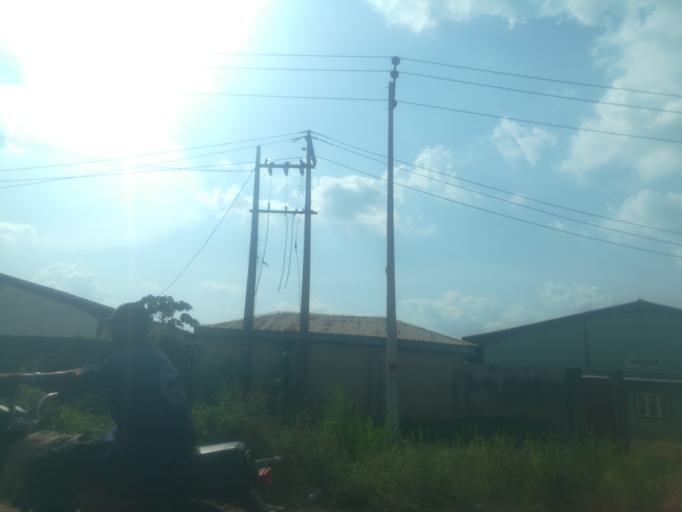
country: NG
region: Ogun
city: Abeokuta
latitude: 7.1143
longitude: 3.2975
